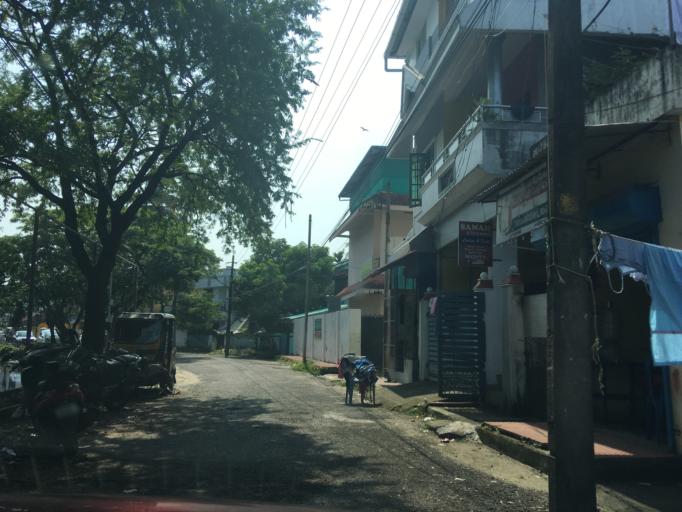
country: IN
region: Kerala
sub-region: Ernakulam
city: Cochin
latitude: 9.9663
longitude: 76.2500
